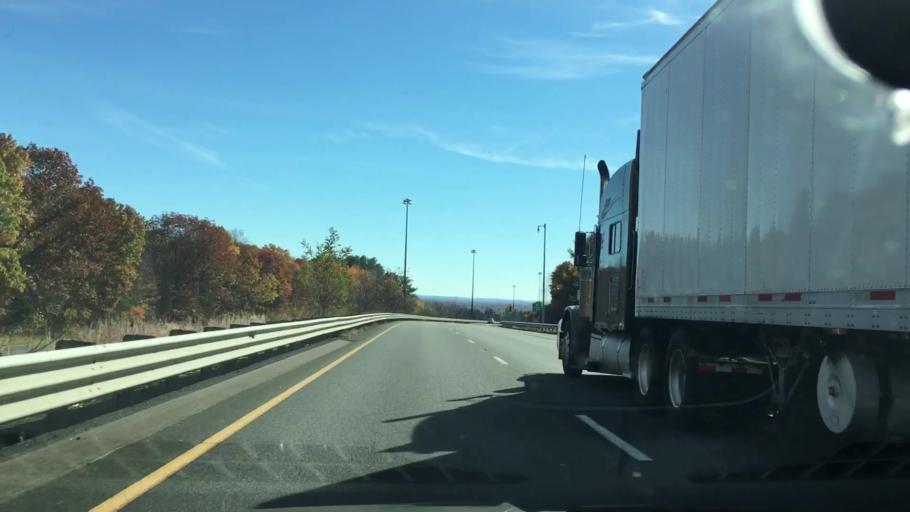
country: US
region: Massachusetts
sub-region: Hampden County
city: Holyoke
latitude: 42.2194
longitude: -72.6343
